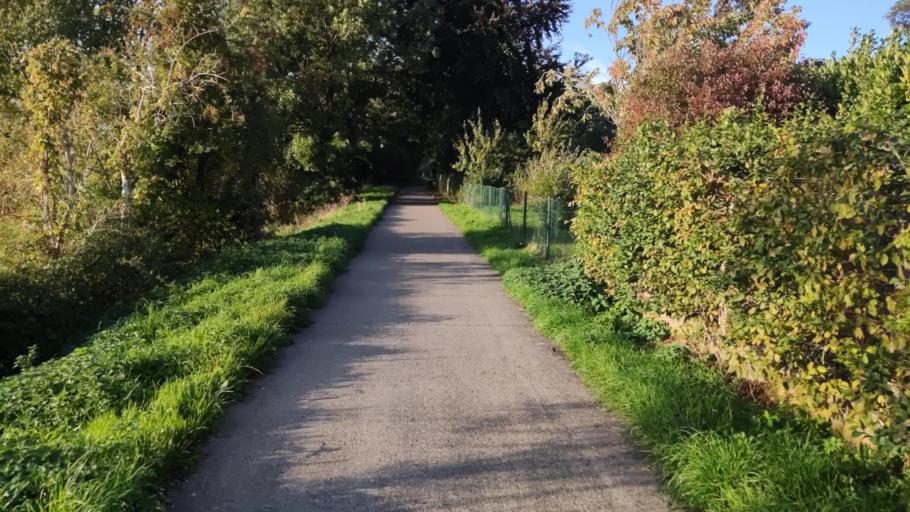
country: BE
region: Wallonia
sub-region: Province du Brabant Wallon
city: Jodoigne
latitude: 50.7402
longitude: 4.8791
